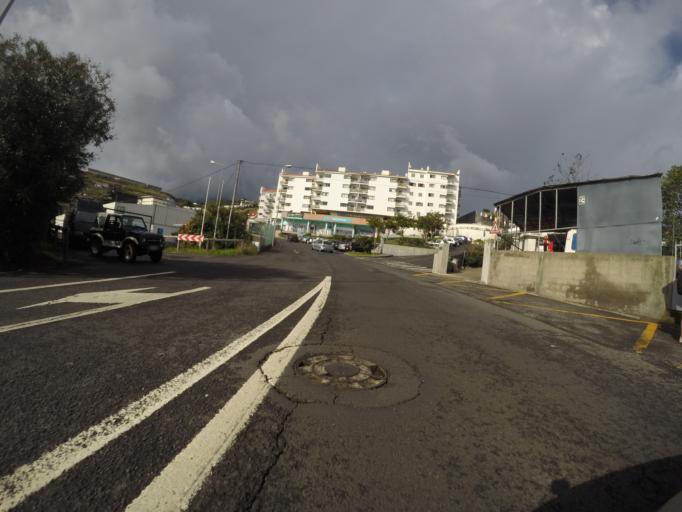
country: PT
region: Madeira
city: Canico
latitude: 32.6456
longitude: -16.8570
